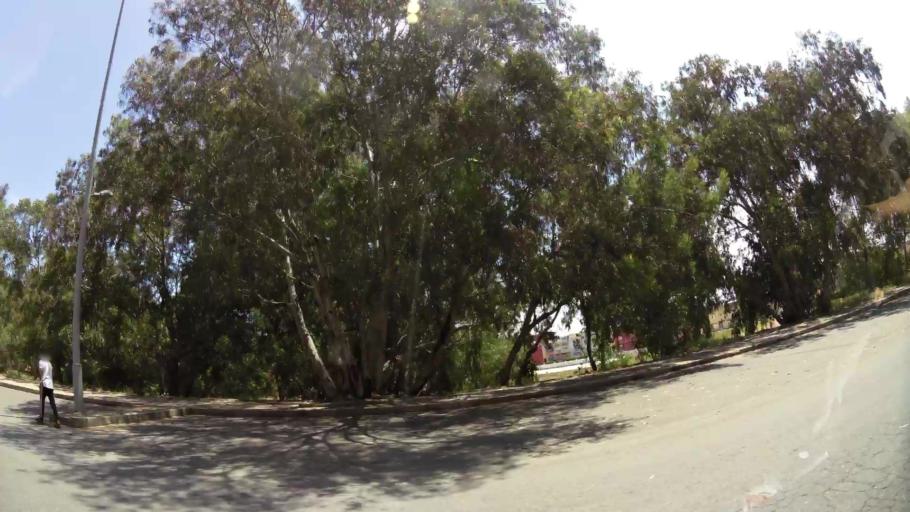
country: MA
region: Gharb-Chrarda-Beni Hssen
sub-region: Kenitra Province
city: Kenitra
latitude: 34.2622
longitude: -6.6126
